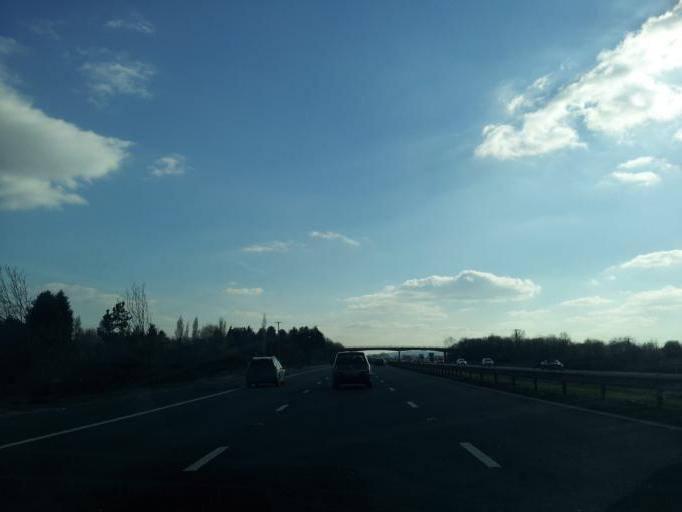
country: GB
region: England
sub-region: North Somerset
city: Kingston Seymour
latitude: 51.4002
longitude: -2.8543
